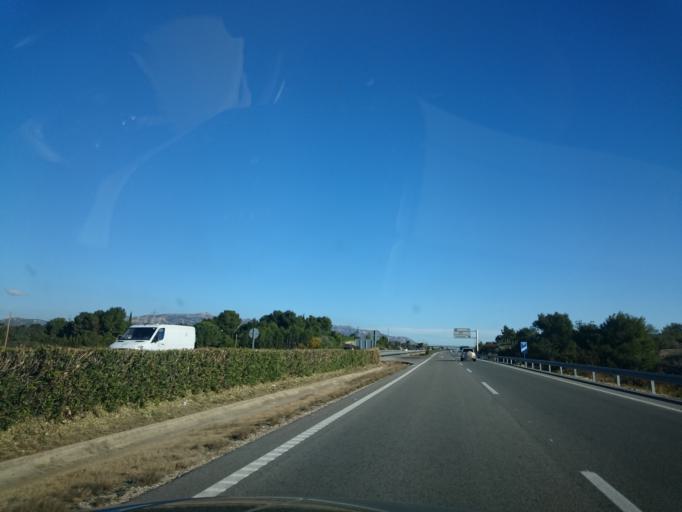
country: ES
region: Catalonia
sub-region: Provincia de Tarragona
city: l'Ametlla de Mar
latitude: 40.8795
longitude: 0.7924
